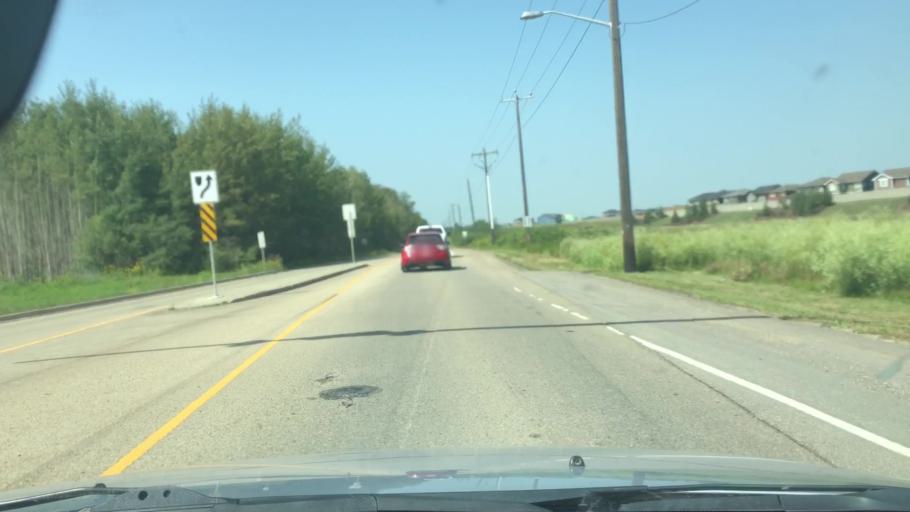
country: CA
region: Alberta
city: St. Albert
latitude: 53.5122
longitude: -113.6906
